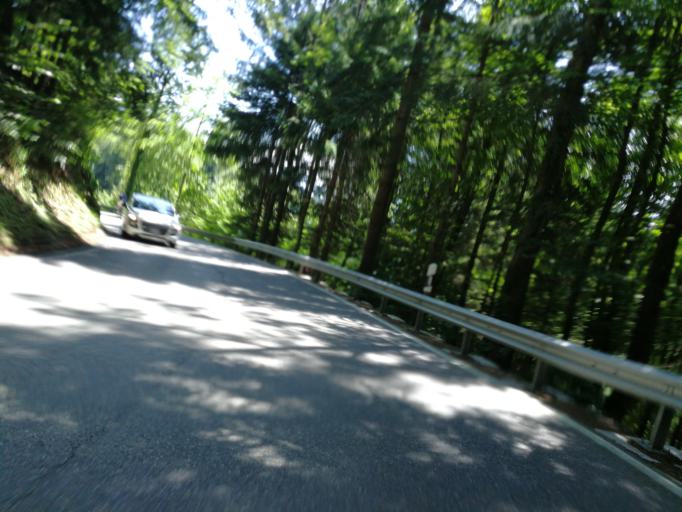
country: CH
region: Saint Gallen
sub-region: Wahlkreis See-Gaster
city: Eschenbach
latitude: 47.2283
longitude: 8.9213
